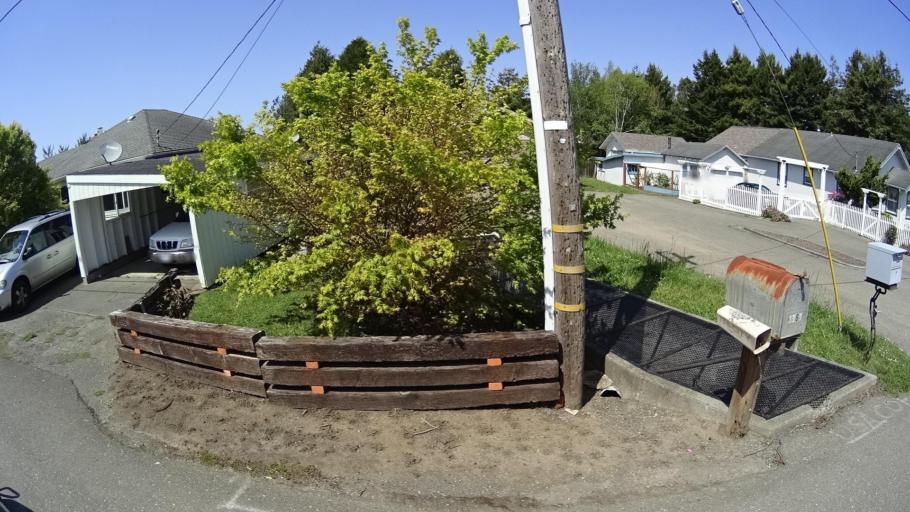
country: US
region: California
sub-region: Humboldt County
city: Hydesville
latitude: 40.5630
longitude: -124.1302
